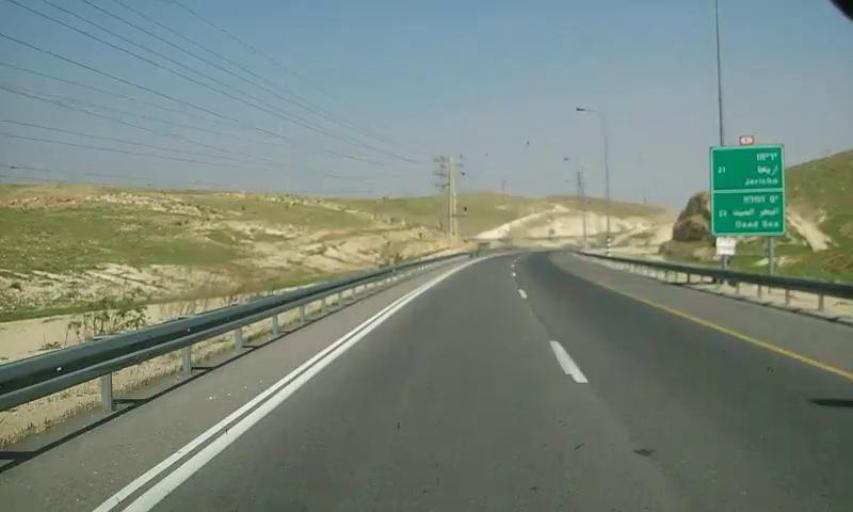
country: PS
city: Az Za`ayyim
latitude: 31.8069
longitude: 35.3285
